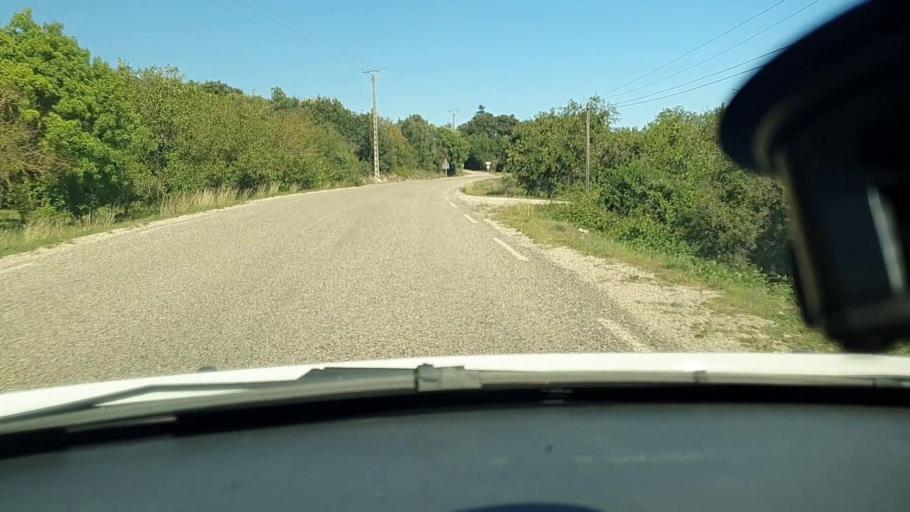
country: FR
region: Languedoc-Roussillon
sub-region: Departement du Gard
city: Goudargues
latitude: 44.1526
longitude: 4.4545
